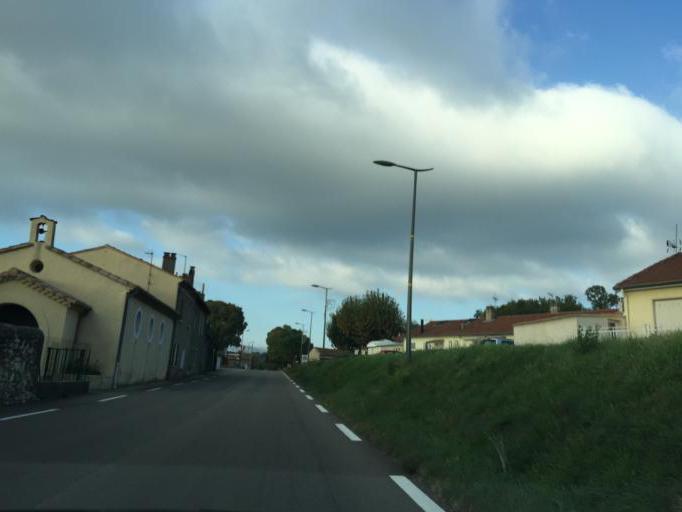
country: FR
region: Rhone-Alpes
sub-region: Departement de la Drome
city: Donzere
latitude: 44.4381
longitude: 4.6687
